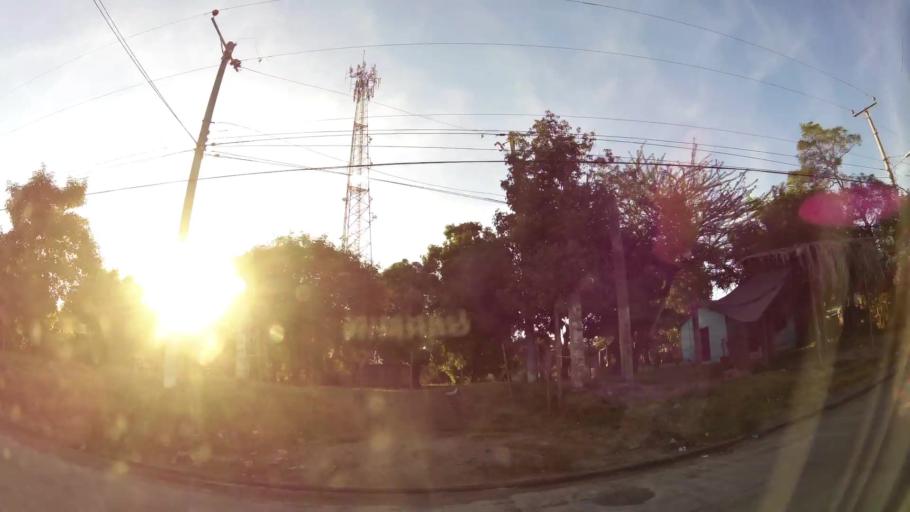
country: SV
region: San Miguel
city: San Miguel
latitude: 13.4582
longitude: -88.1768
